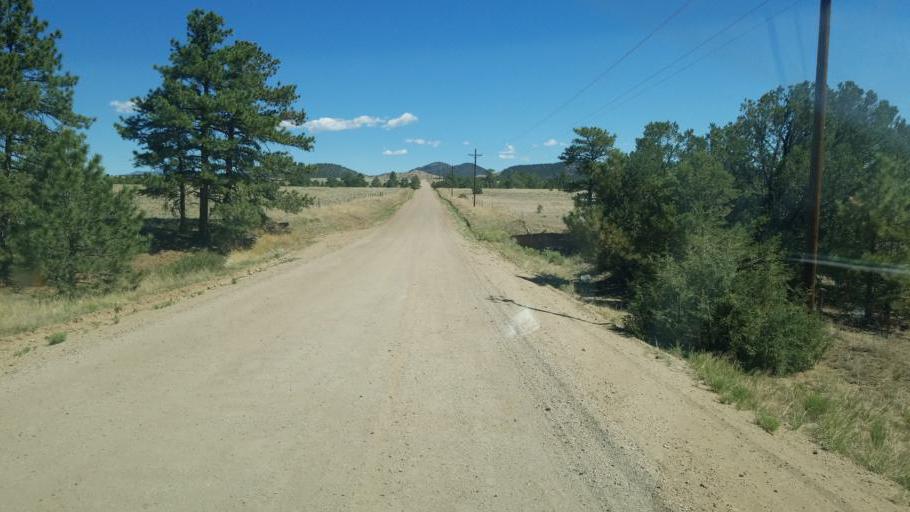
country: US
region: Colorado
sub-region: Custer County
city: Westcliffe
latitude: 38.2714
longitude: -105.5010
